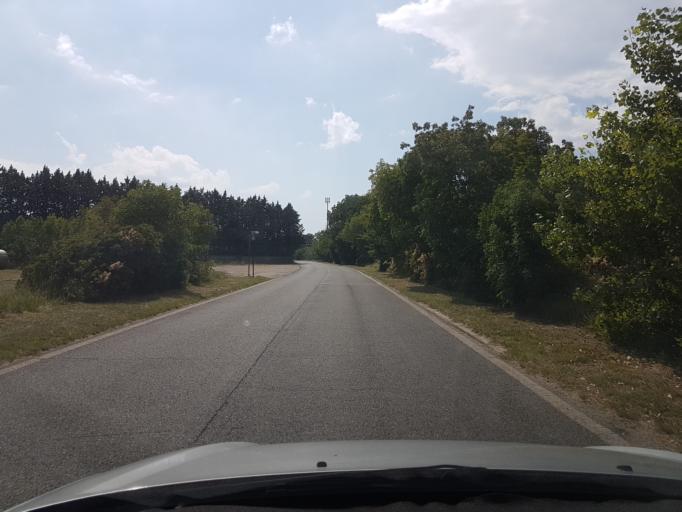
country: IT
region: Friuli Venezia Giulia
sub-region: Provincia di Trieste
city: Prosecco-Contovello
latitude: 45.7051
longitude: 13.7570
